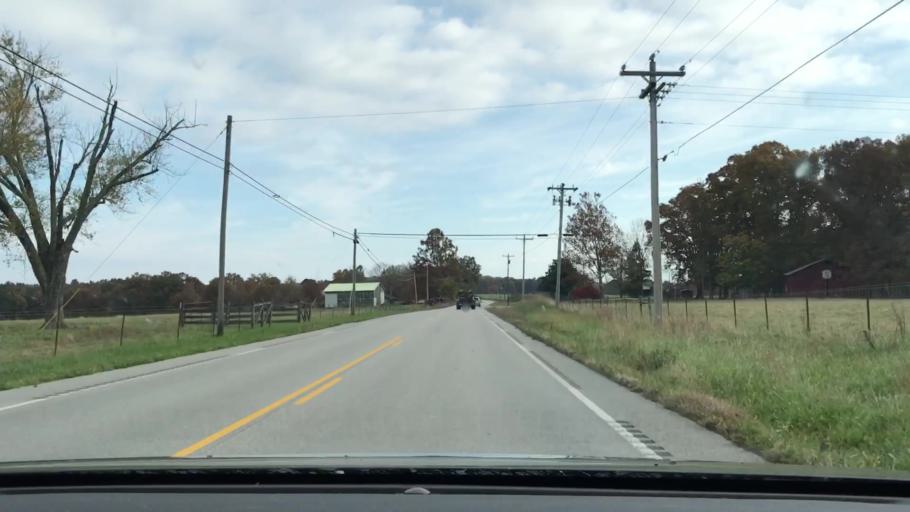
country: US
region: Tennessee
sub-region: Fentress County
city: Jamestown
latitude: 36.3632
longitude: -84.8118
